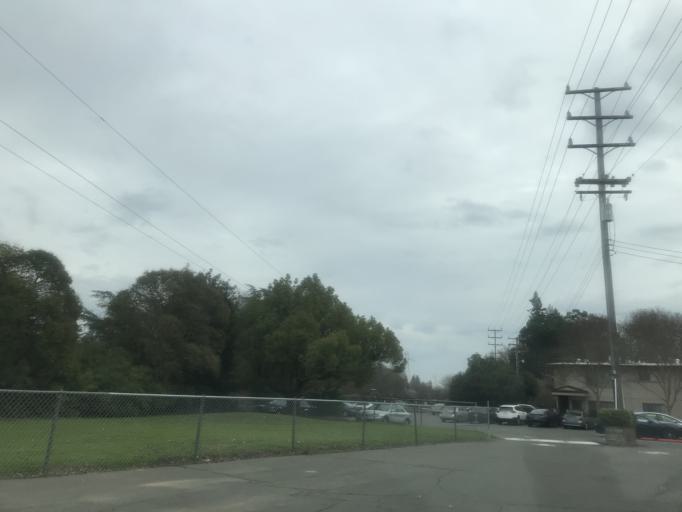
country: US
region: California
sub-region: Sacramento County
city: Arden-Arcade
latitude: 38.5828
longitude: -121.4136
